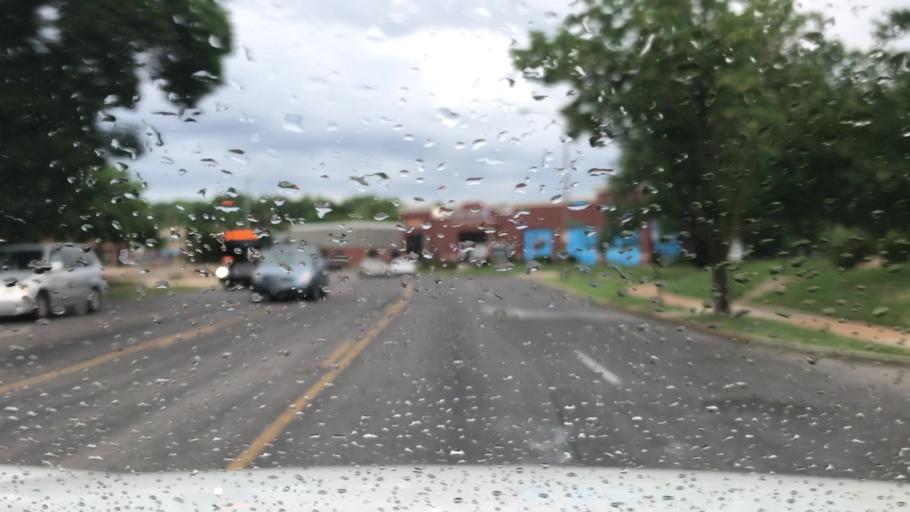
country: US
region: Missouri
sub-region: Saint Louis County
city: Maplewood
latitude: 38.5938
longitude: -90.2978
